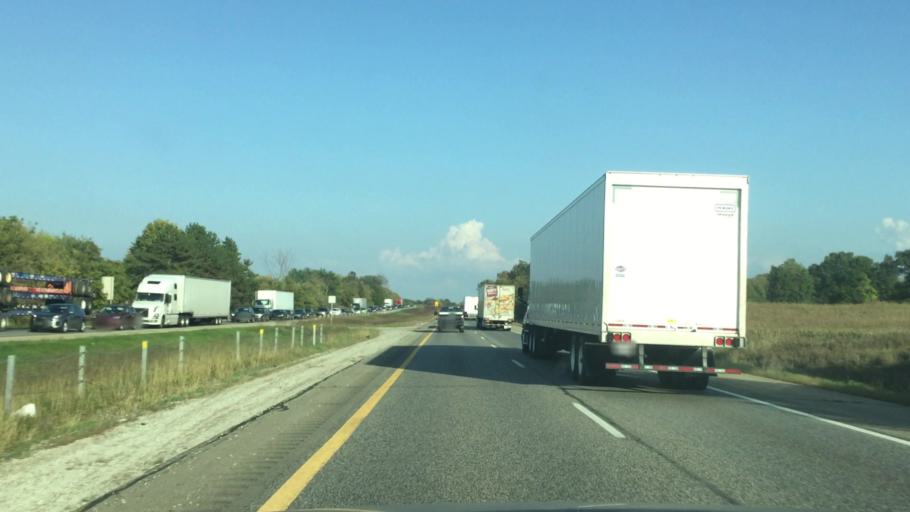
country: US
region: Michigan
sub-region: Washtenaw County
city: Chelsea
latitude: 42.2977
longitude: -84.1067
